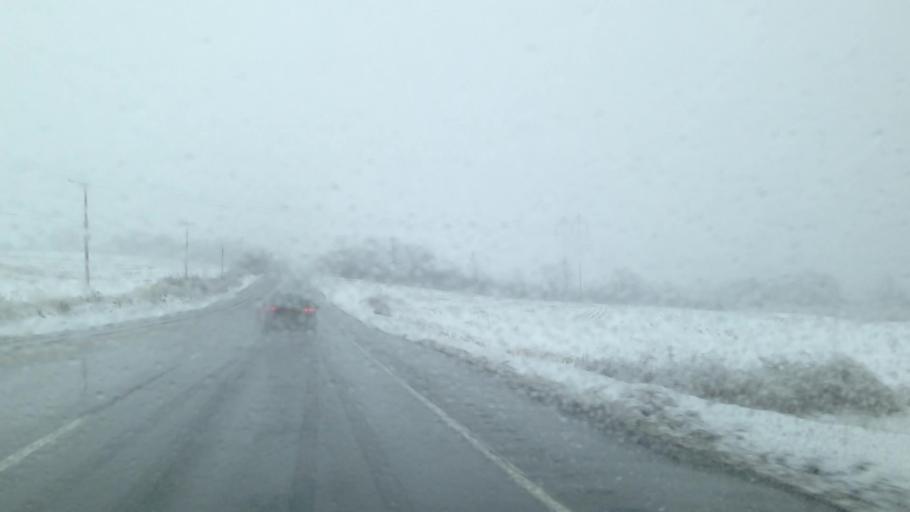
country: US
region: New York
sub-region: Onondaga County
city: Peru
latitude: 43.0363
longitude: -76.3923
